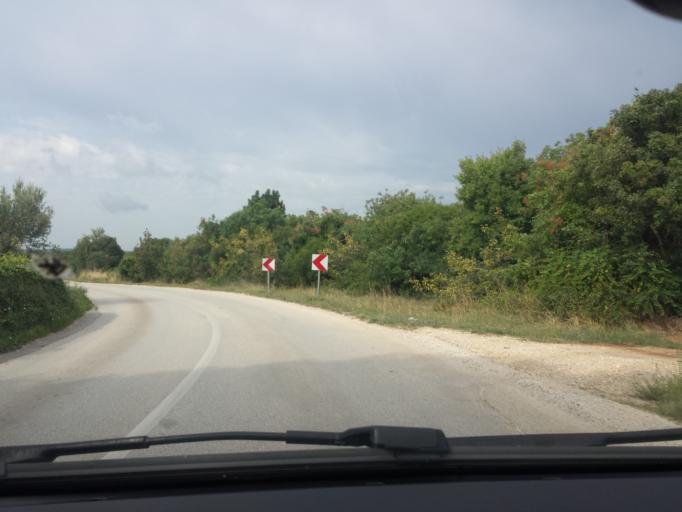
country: HR
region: Istarska
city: Galizana
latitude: 44.9234
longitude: 13.8617
